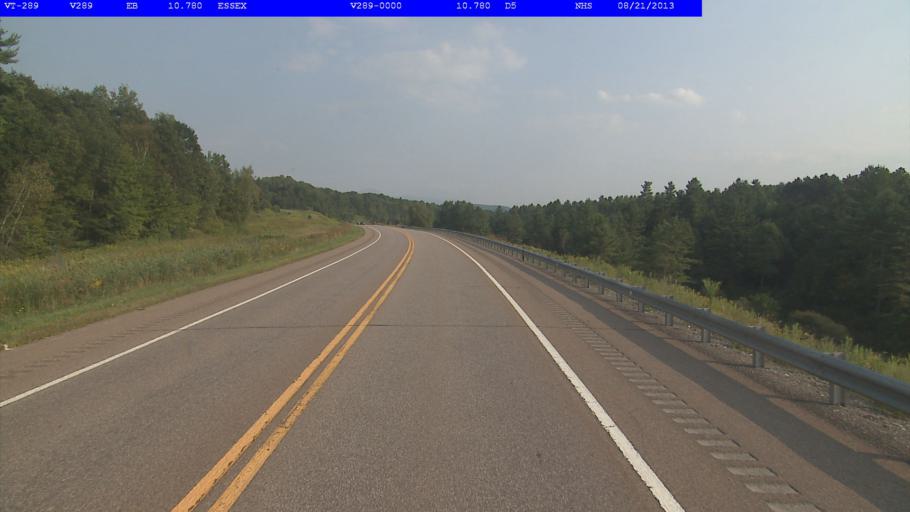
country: US
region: Vermont
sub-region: Chittenden County
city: Essex Junction
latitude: 44.4961
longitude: -73.0687
